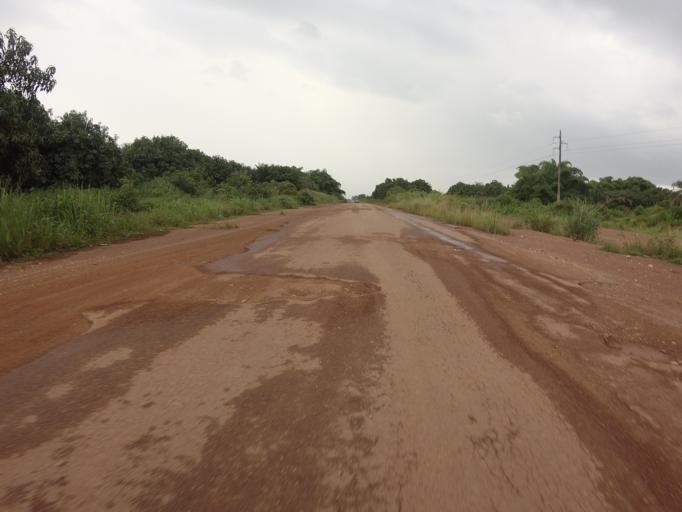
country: GH
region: Volta
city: Kpandu
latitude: 7.0194
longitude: 0.4281
